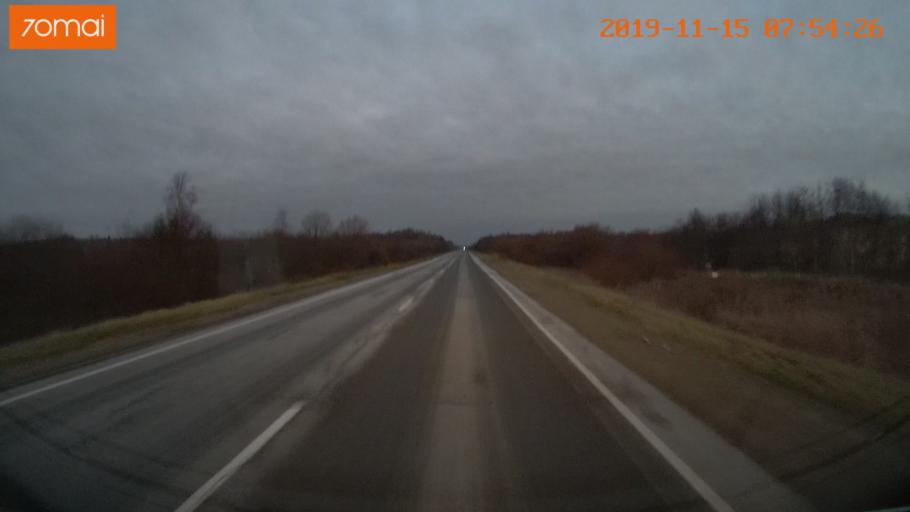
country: RU
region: Vologda
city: Cherepovets
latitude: 58.8986
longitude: 38.1758
